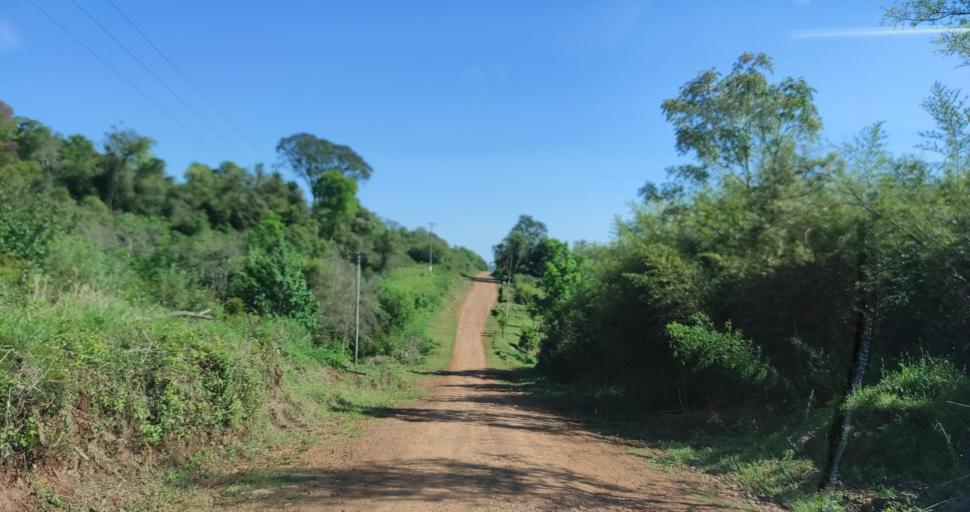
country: AR
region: Misiones
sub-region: Departamento de Candelaria
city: Loreto
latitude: -27.3186
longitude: -55.5328
